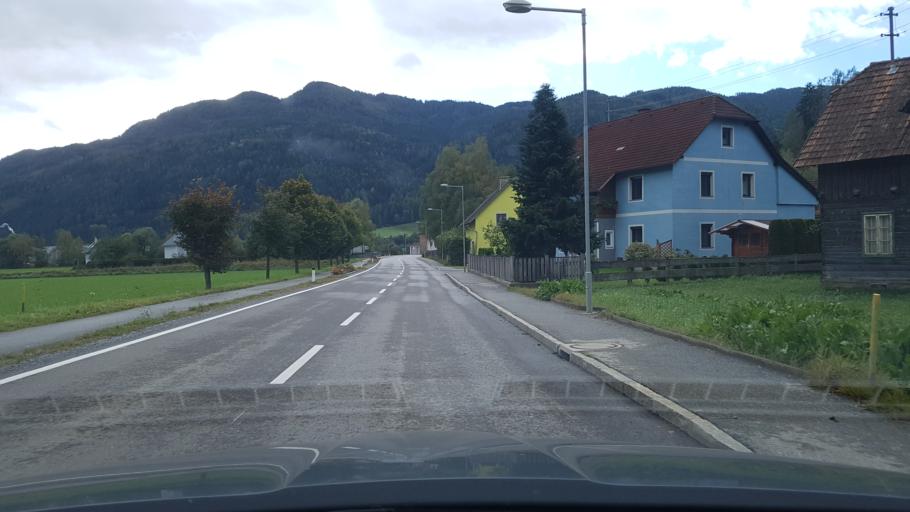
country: AT
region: Styria
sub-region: Politischer Bezirk Murau
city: Triebendorf
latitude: 47.1417
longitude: 14.2839
